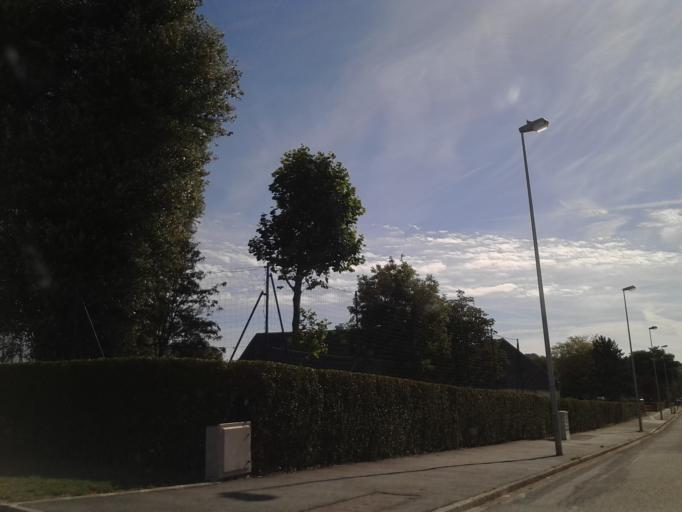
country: FR
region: Lower Normandy
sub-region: Departement de la Manche
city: Tourlaville
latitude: 49.6440
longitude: -1.5802
